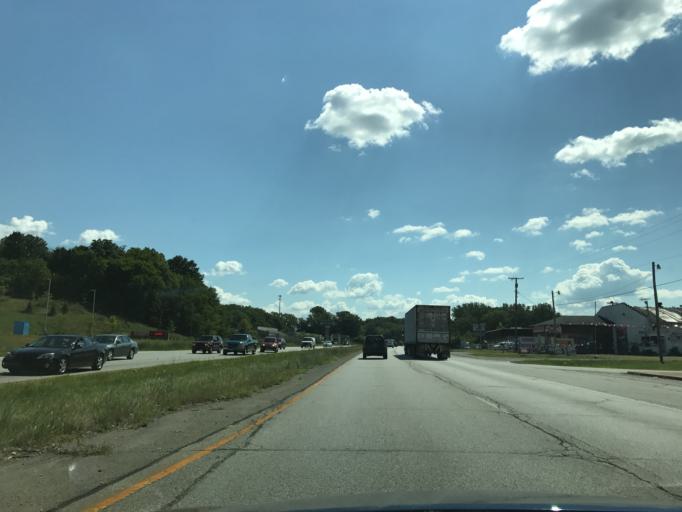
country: US
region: Indiana
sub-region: Porter County
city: Valparaiso
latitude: 41.4592
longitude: -87.0634
